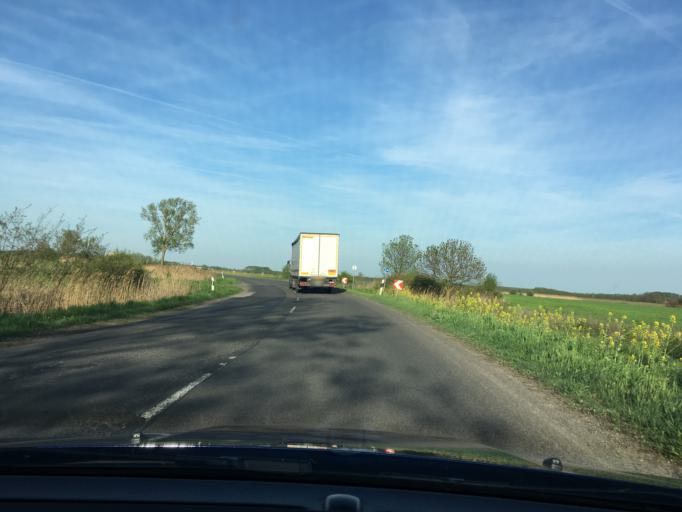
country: HU
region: Bekes
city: Korosladany
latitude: 47.0006
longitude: 21.1134
